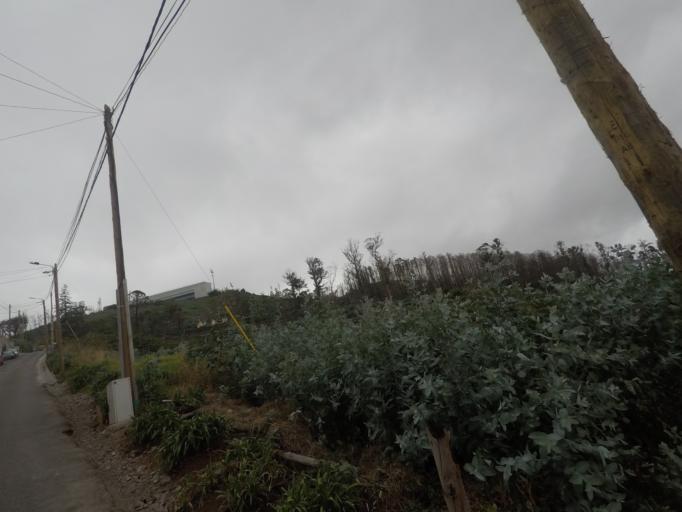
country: PT
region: Madeira
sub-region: Funchal
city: Nossa Senhora do Monte
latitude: 32.6684
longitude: -16.8886
